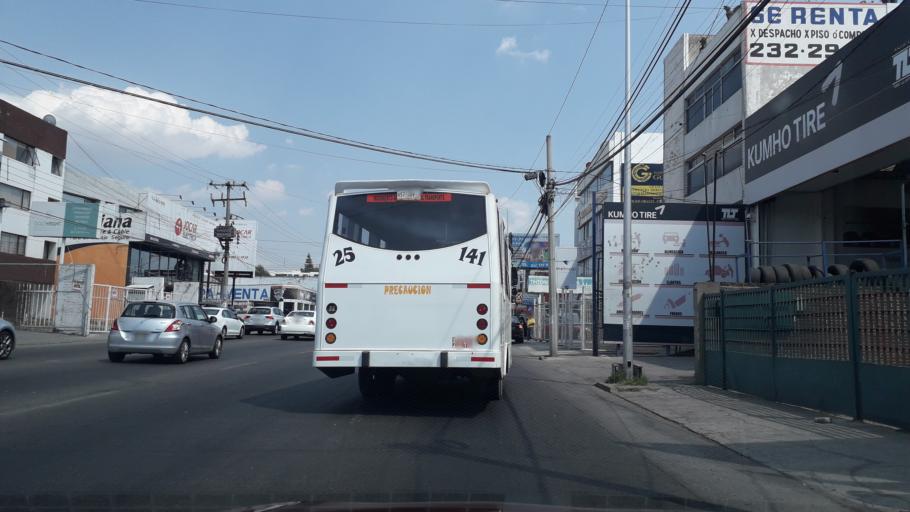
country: MX
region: Puebla
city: Puebla
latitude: 19.0279
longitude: -98.2216
